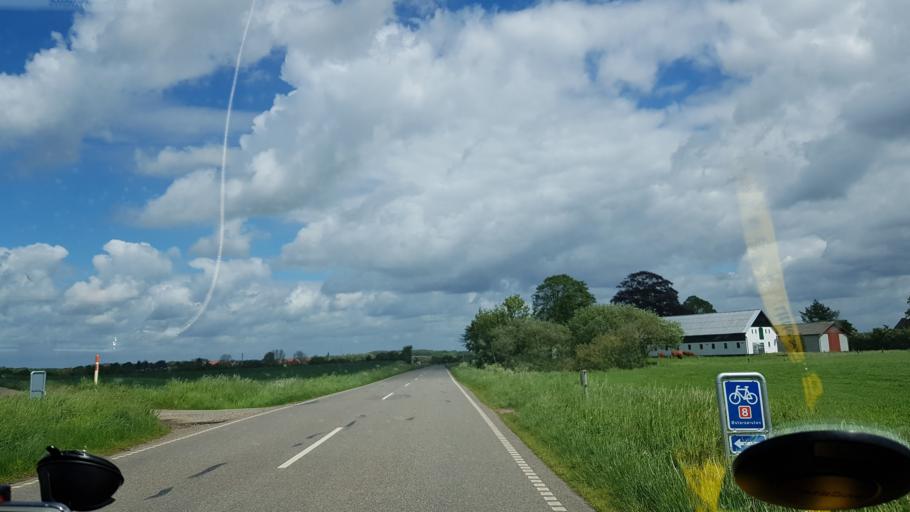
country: DK
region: South Denmark
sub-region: Kolding Kommune
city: Christiansfeld
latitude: 55.3416
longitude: 9.4675
